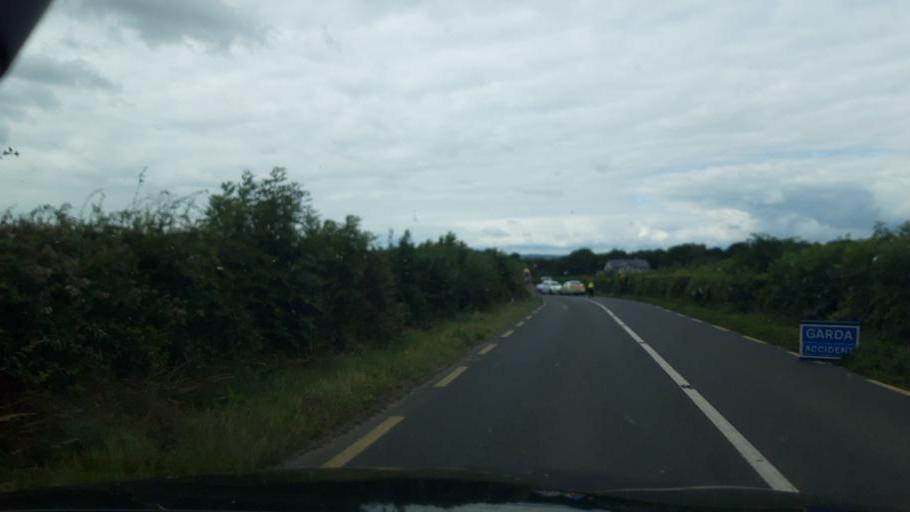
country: IE
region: Leinster
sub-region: Kilkenny
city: Thomastown
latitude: 52.6230
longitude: -7.0701
